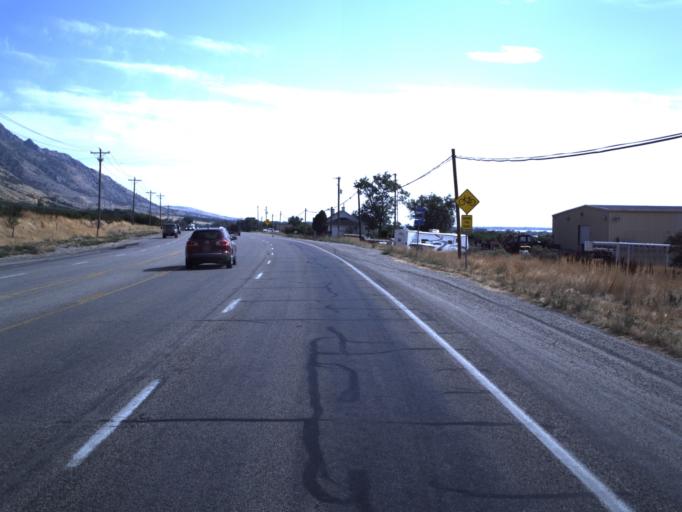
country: US
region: Utah
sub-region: Box Elder County
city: Perry
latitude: 41.4549
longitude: -112.0388
